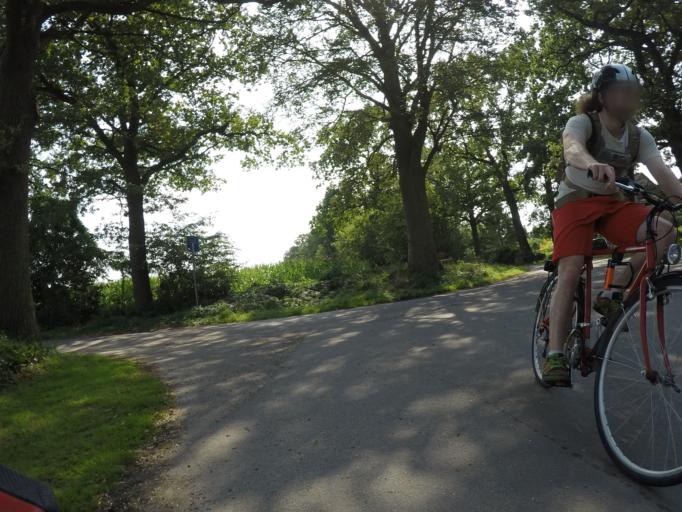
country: DE
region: Schleswig-Holstein
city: Kisdorf
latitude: 53.7756
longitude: 10.0470
